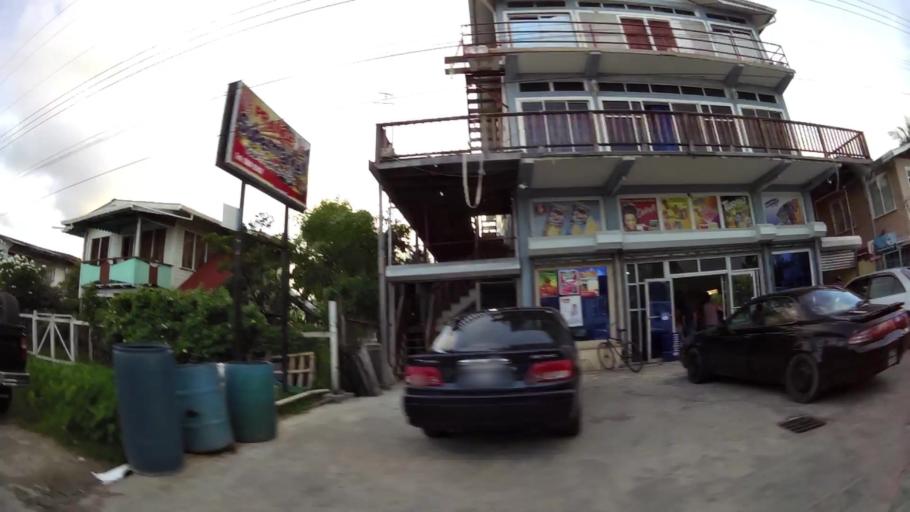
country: GY
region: Demerara-Mahaica
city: Georgetown
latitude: 6.8157
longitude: -58.1075
